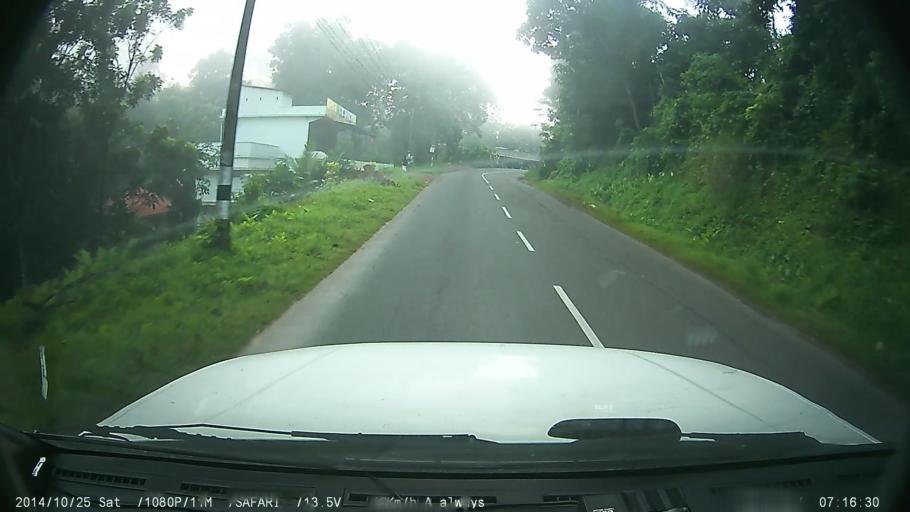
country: IN
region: Kerala
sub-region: Kottayam
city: Palackattumala
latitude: 9.8179
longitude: 76.5866
